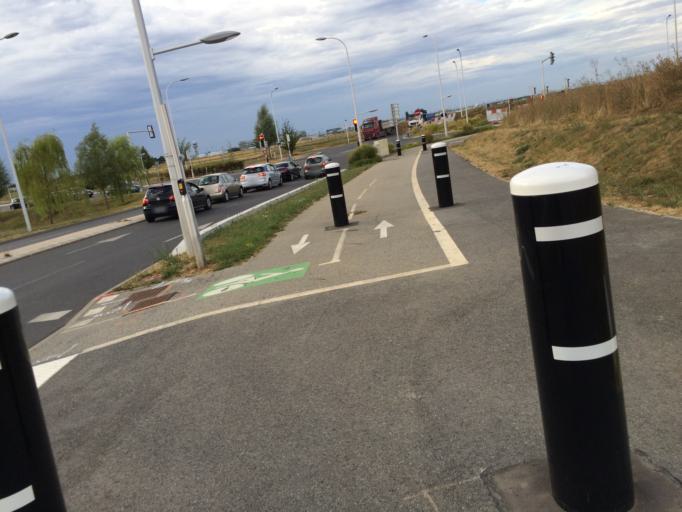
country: FR
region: Ile-de-France
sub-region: Departement de l'Essonne
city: Athis-Mons
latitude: 48.7130
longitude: 2.3784
